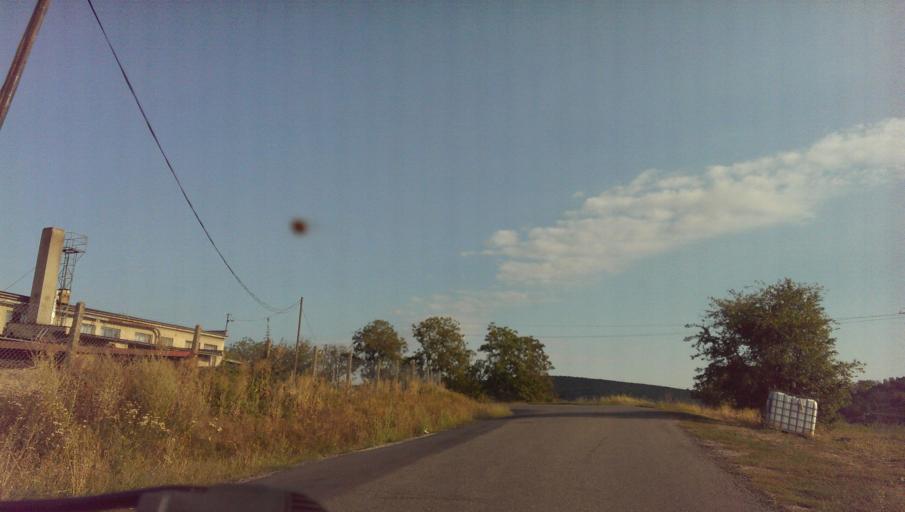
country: CZ
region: South Moravian
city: Zeravice
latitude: 49.0550
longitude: 17.2454
